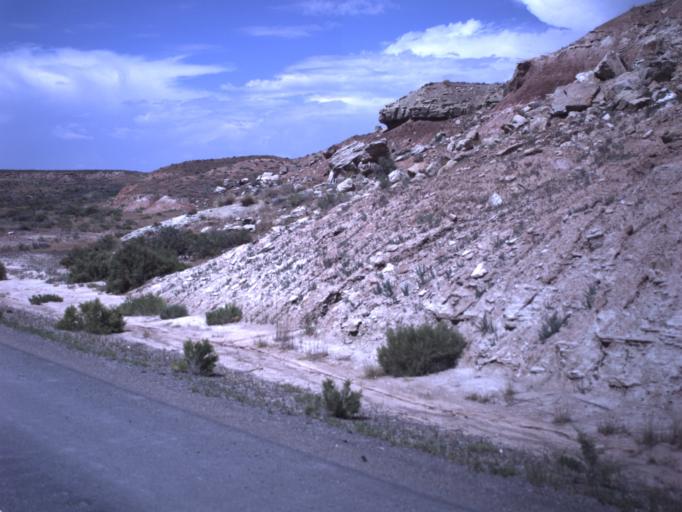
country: US
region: Utah
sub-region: Uintah County
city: Maeser
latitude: 40.3130
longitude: -109.7044
